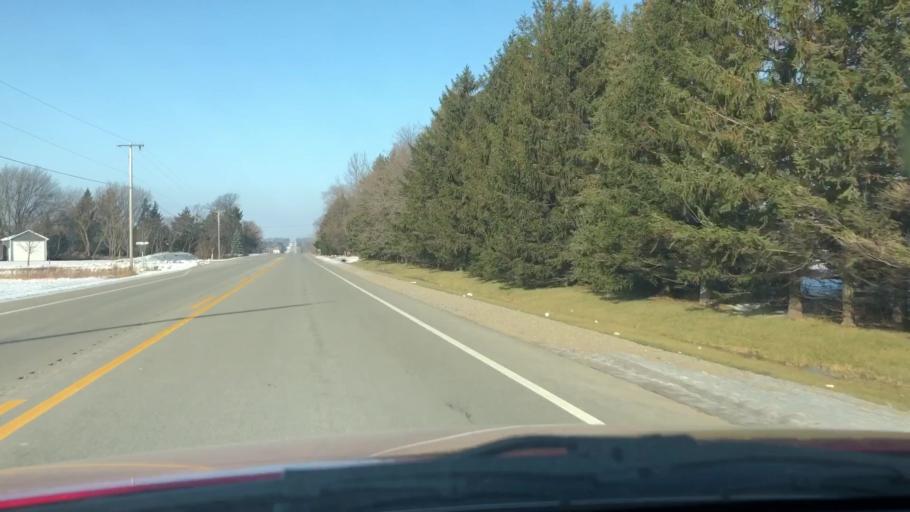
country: US
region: Wisconsin
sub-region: Outagamie County
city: Kimberly
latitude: 44.3492
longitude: -88.3749
